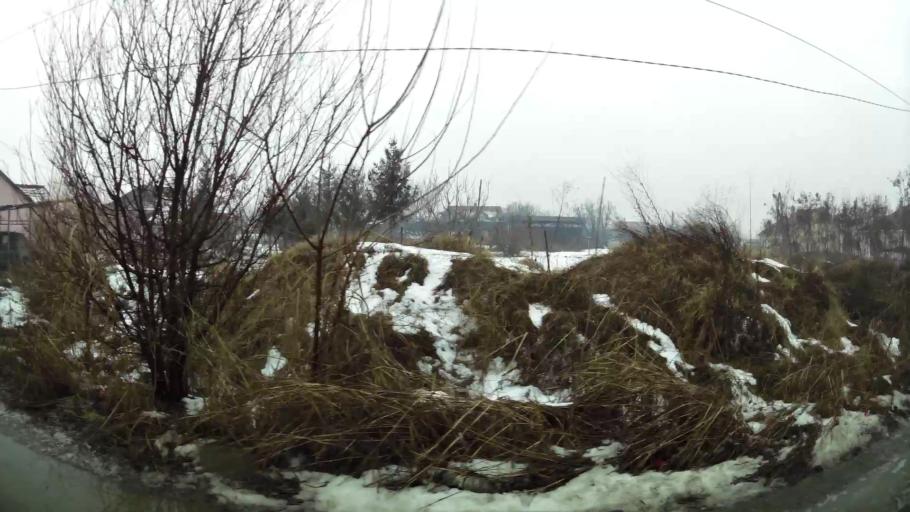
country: MK
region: Petrovec
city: Petrovec
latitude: 41.9360
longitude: 21.6169
